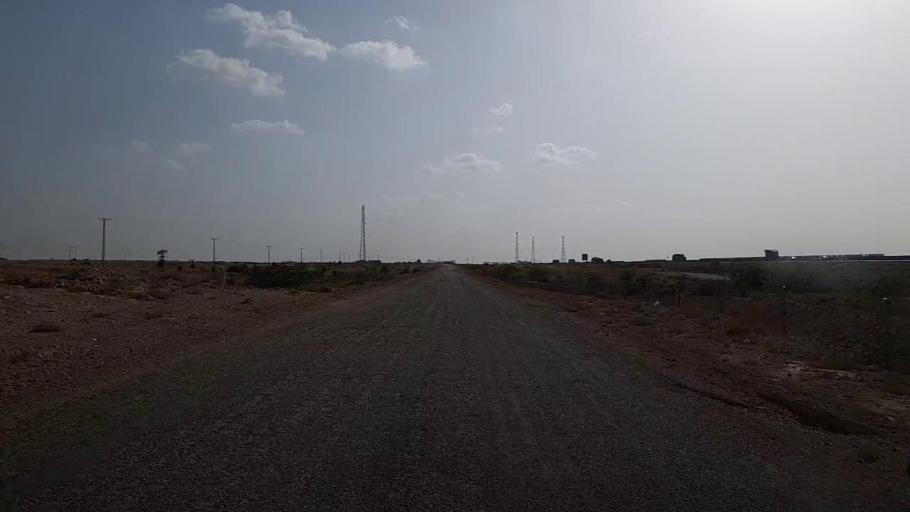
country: PK
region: Sindh
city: Kotri
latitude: 25.2584
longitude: 67.9731
